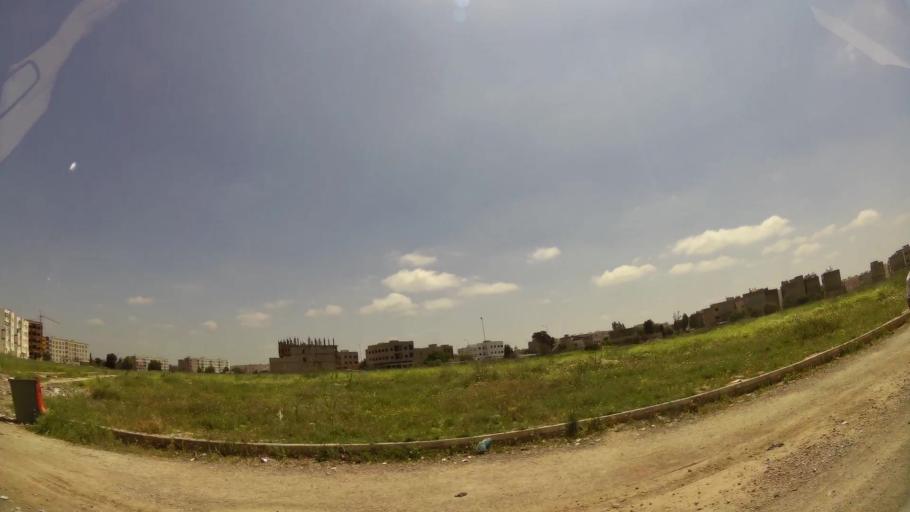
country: MA
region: Fes-Boulemane
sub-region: Fes
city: Fes
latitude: 34.0235
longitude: -5.0436
